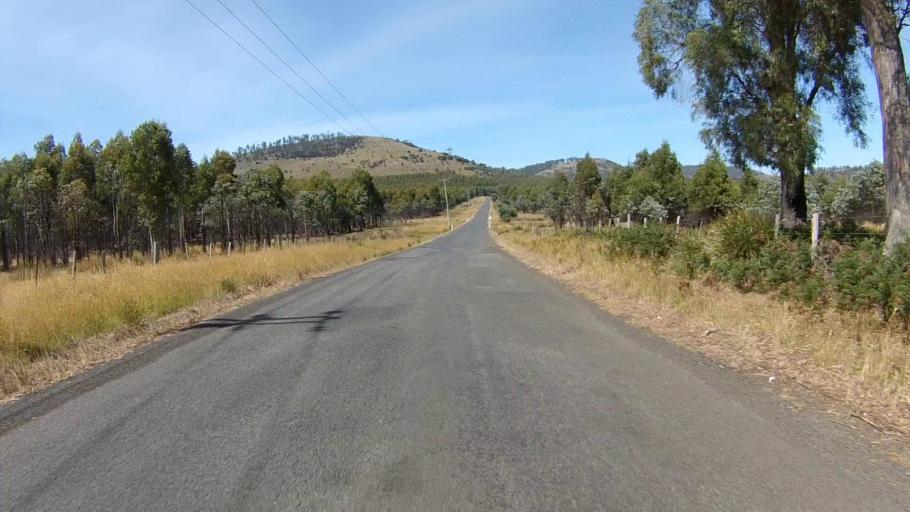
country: AU
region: Tasmania
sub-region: Sorell
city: Sorell
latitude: -42.6188
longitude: 147.7302
